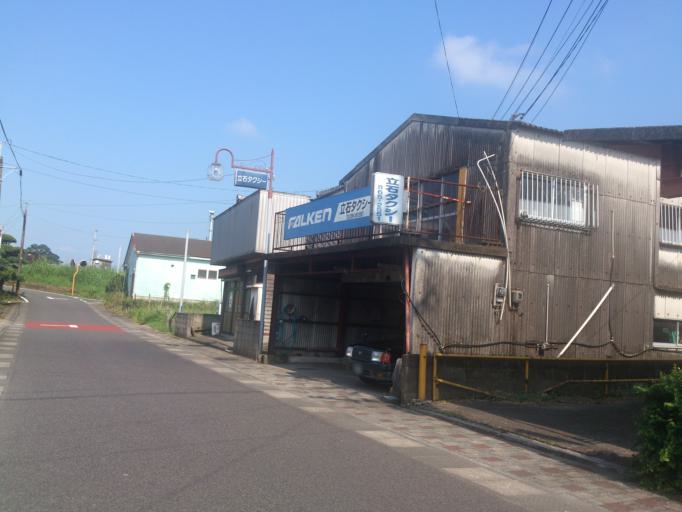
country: JP
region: Kagoshima
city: Kanoya
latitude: 31.3468
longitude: 130.9446
